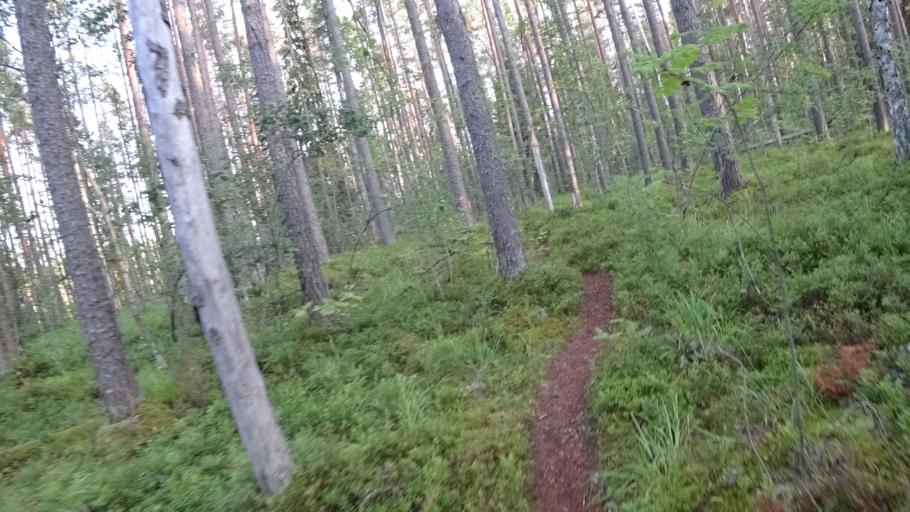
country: FI
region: North Karelia
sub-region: Joensuu
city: Ilomantsi
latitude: 62.5819
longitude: 31.1666
